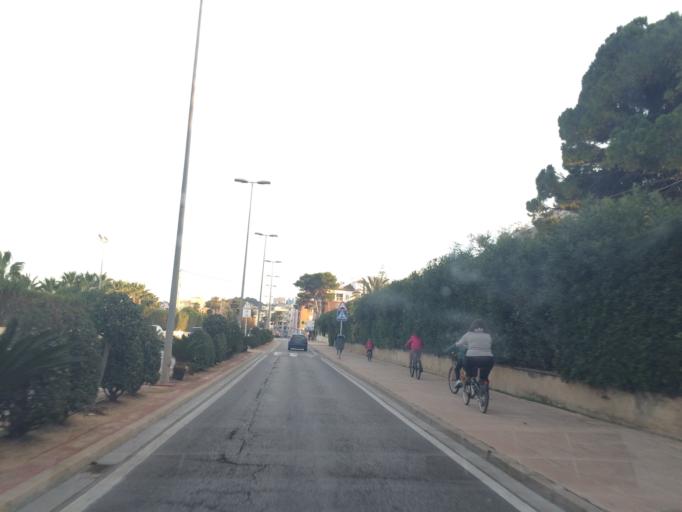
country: ES
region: Valencia
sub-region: Provincia de Alicante
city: Denia
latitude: 38.8378
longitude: 0.1159
